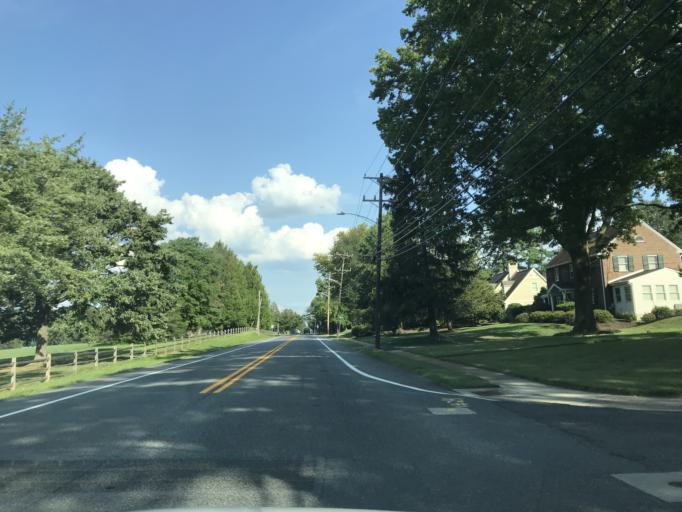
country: US
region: Delaware
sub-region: New Castle County
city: Newark
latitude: 39.6874
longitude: -75.7679
